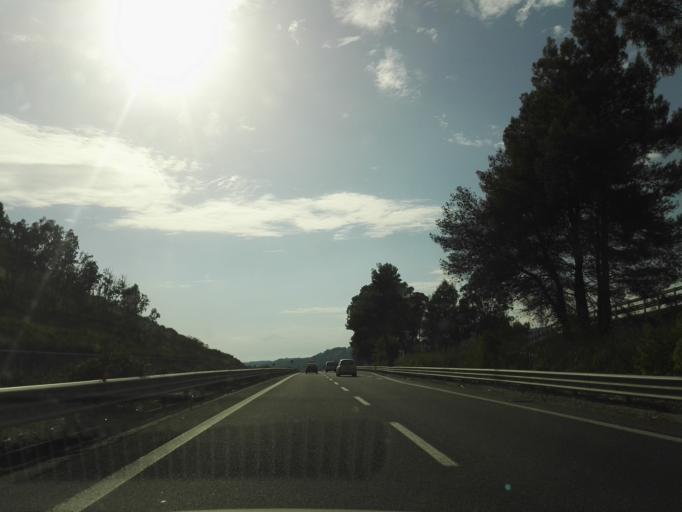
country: IT
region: Calabria
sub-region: Provincia di Catanzaro
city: Marcellinara
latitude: 38.9180
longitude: 16.4817
